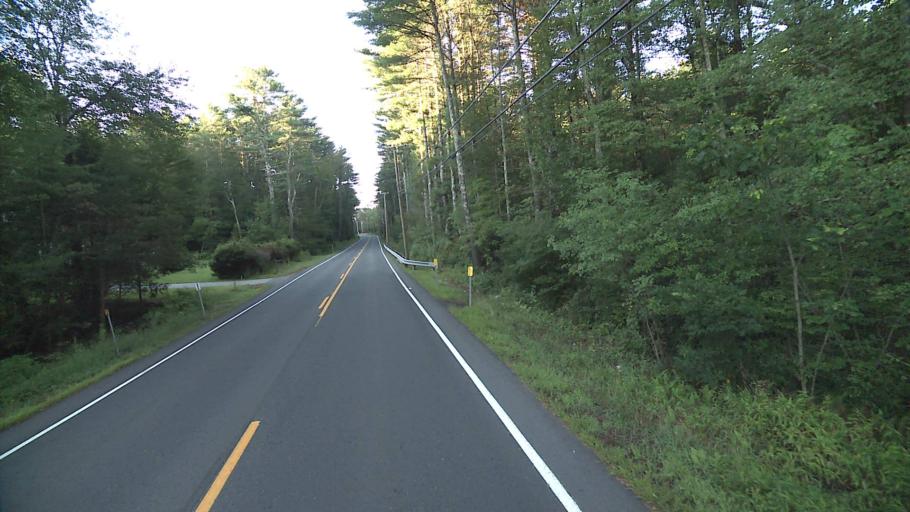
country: US
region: Connecticut
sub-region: Tolland County
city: Stafford
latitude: 42.0078
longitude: -72.3179
